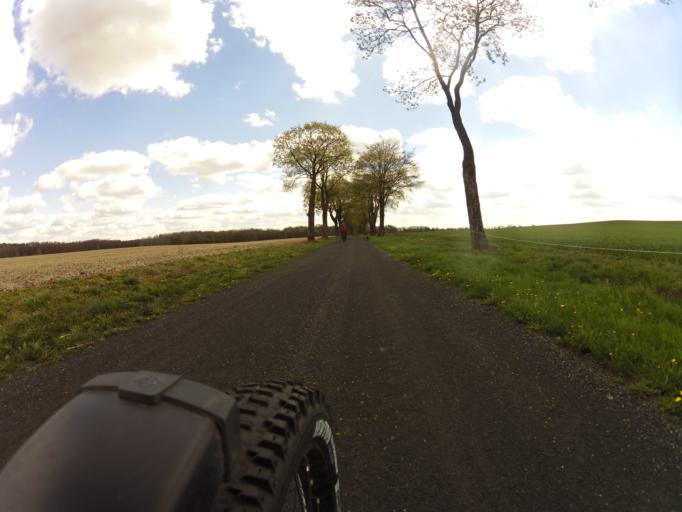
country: PL
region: West Pomeranian Voivodeship
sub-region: Powiat gryficki
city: Gryfice
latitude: 53.8522
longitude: 15.1694
